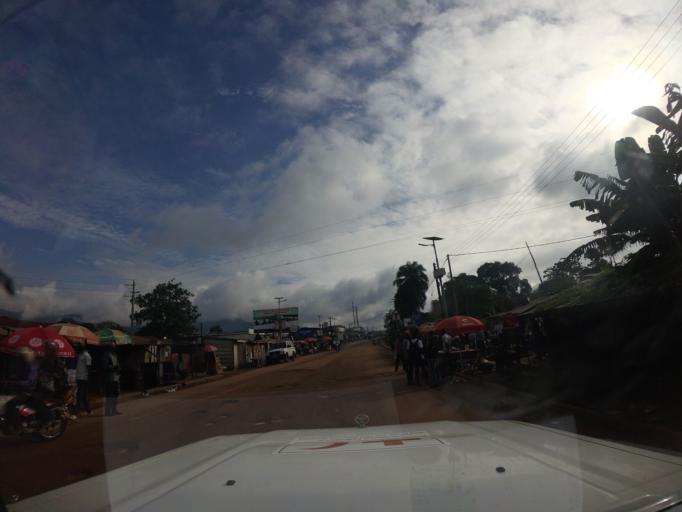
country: SL
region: Eastern Province
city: Kenema
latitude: 7.8807
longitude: -11.1904
